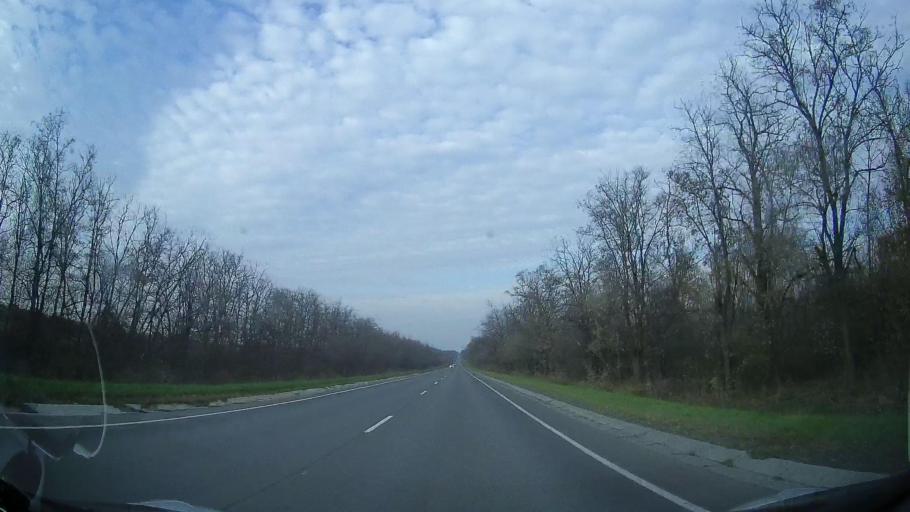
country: RU
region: Rostov
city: Bagayevskaya
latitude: 47.1054
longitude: 40.2767
